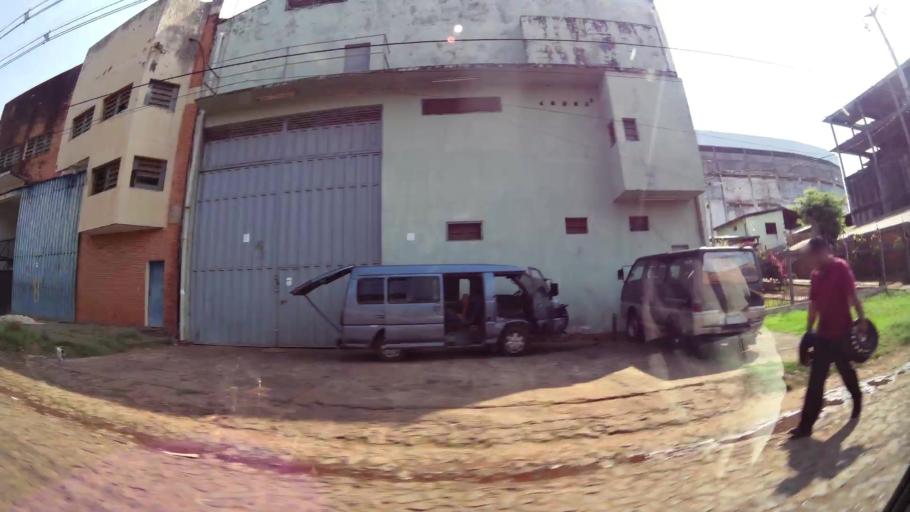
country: PY
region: Alto Parana
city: Ciudad del Este
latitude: -25.5060
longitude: -54.6212
